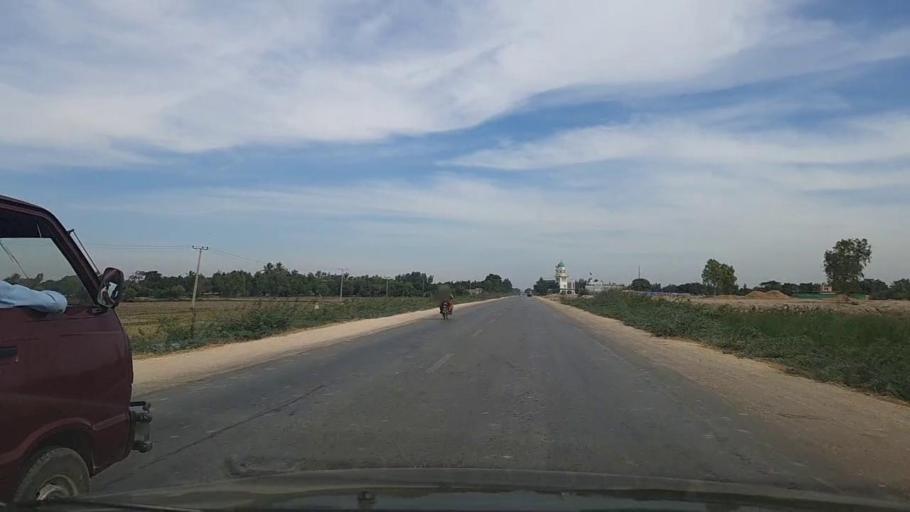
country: PK
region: Sindh
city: Thatta
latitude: 24.7825
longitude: 67.9496
